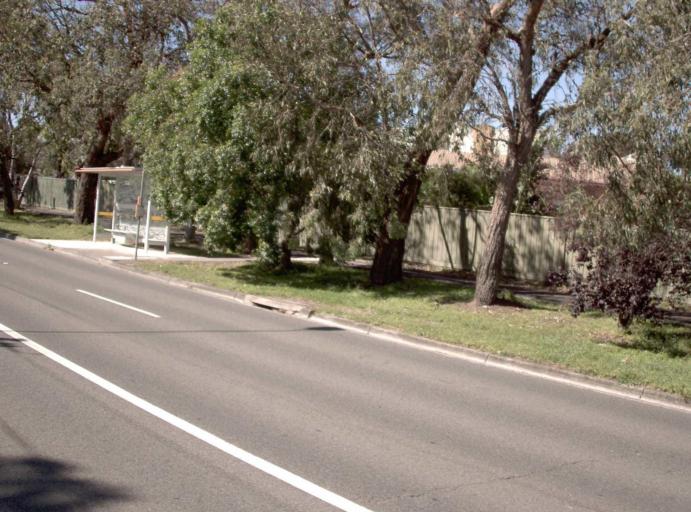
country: AU
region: Victoria
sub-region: Knox
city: Knoxfield
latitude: -37.8800
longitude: 145.2575
